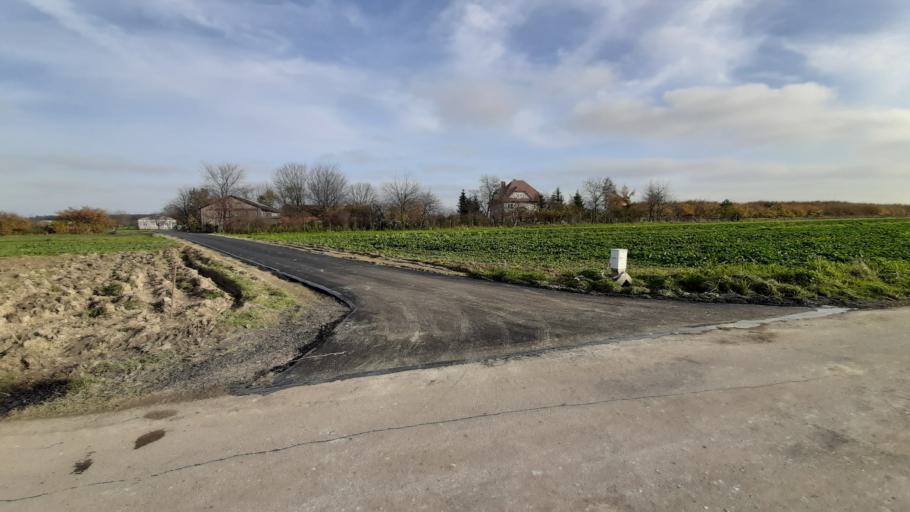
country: PL
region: Lublin Voivodeship
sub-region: Powiat lubelski
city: Jastkow
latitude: 51.3588
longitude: 22.4055
